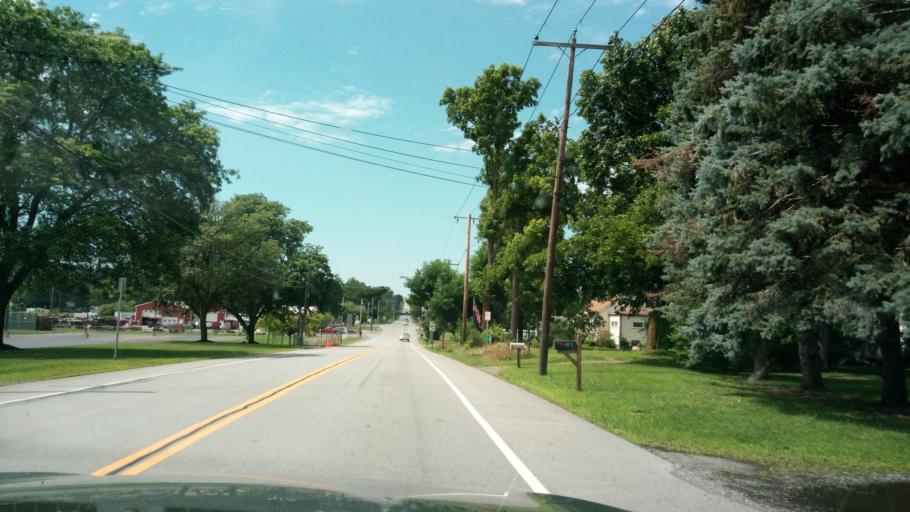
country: US
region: New York
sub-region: Livingston County
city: Geneseo
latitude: 42.8307
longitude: -77.8938
